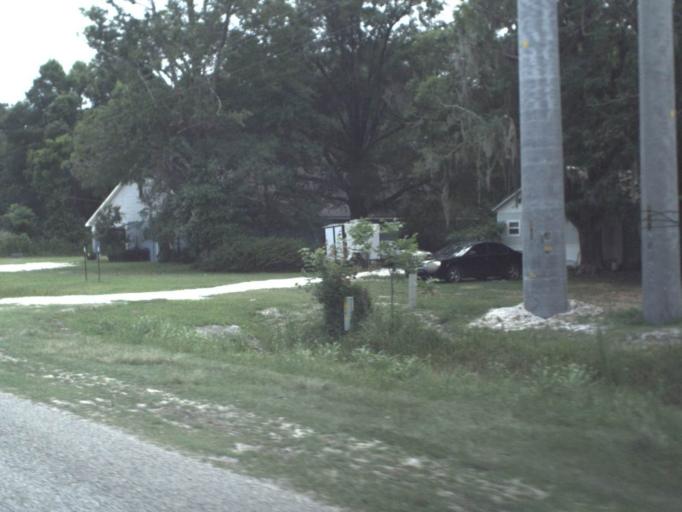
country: US
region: Florida
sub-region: Bradford County
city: Starke
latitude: 29.9906
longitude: -82.0951
